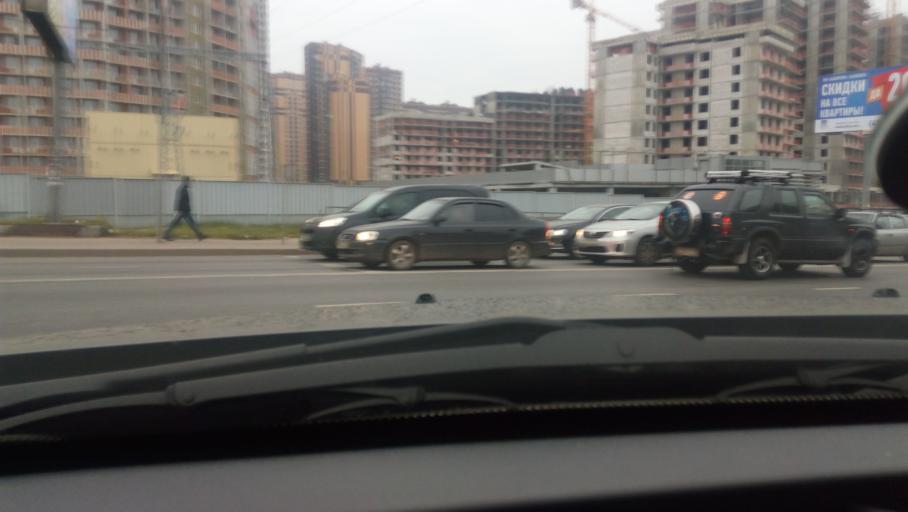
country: RU
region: Moskovskaya
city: Reutov
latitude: 55.7492
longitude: 37.8836
